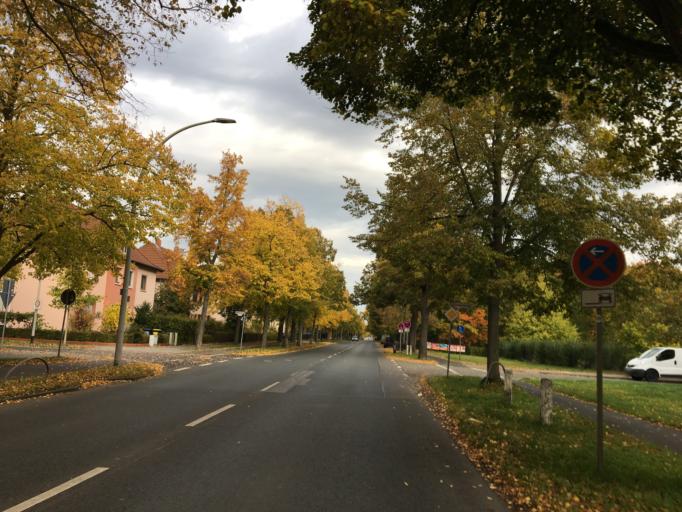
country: DE
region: Lower Saxony
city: Braunschweig
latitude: 52.2882
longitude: 10.5390
